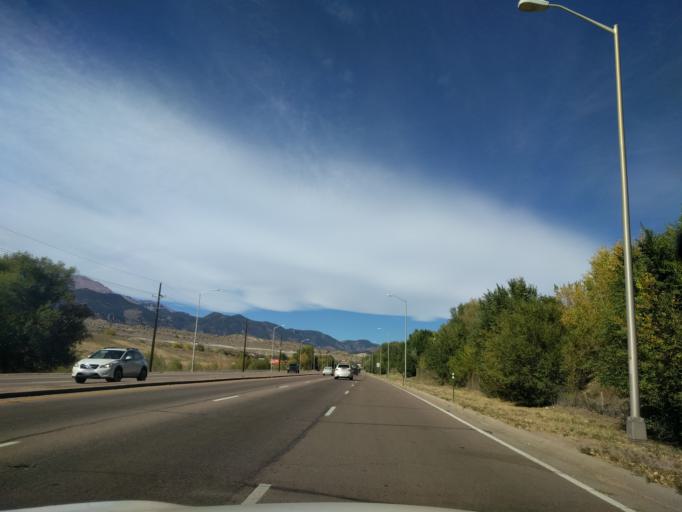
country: US
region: Colorado
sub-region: El Paso County
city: Colorado Springs
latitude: 38.8360
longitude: -104.8501
